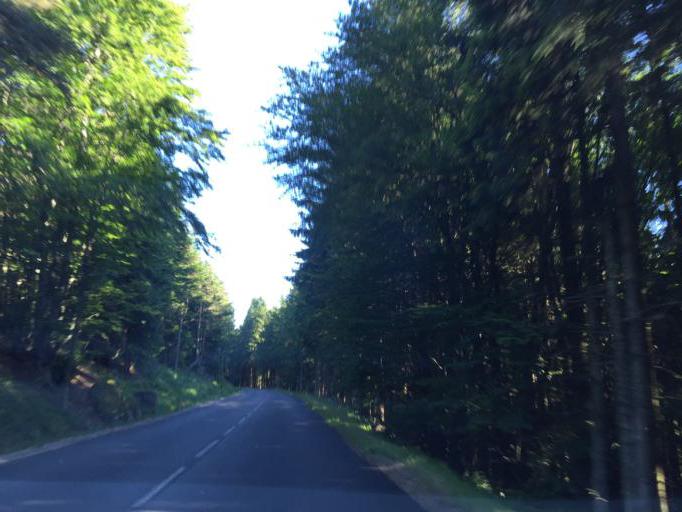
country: FR
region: Rhone-Alpes
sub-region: Departement de la Loire
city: Bourg-Argental
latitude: 45.3736
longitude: 4.5275
